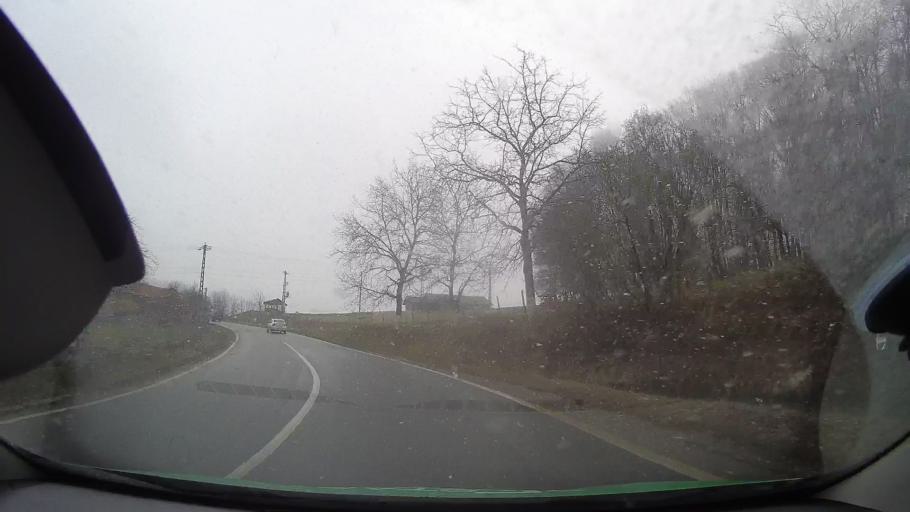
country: RO
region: Sibiu
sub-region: Municipiul Medias
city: Medias
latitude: 46.1842
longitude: 24.3245
